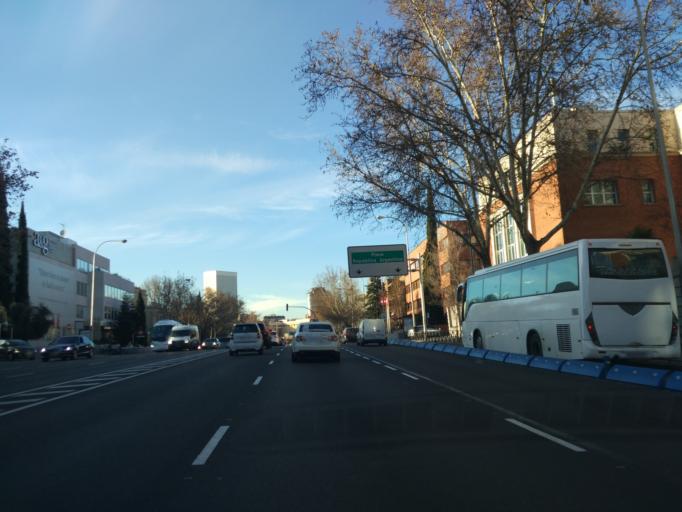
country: ES
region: Madrid
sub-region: Provincia de Madrid
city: Salamanca
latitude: 40.4430
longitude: -3.6832
